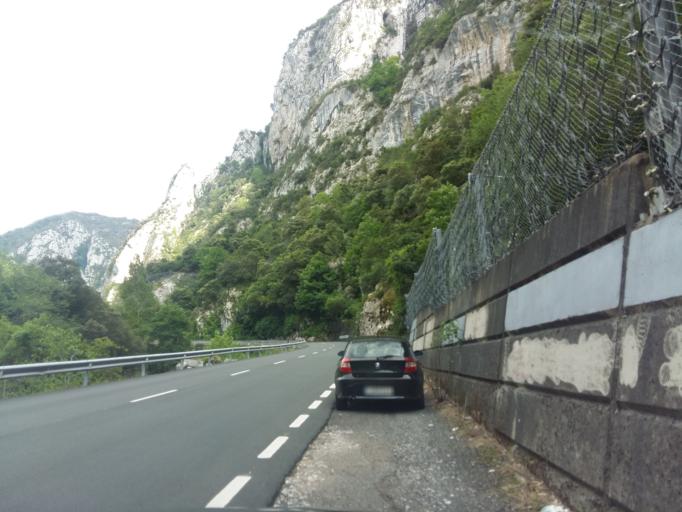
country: ES
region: Cantabria
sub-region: Provincia de Cantabria
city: Tresviso
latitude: 43.2503
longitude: -4.6023
